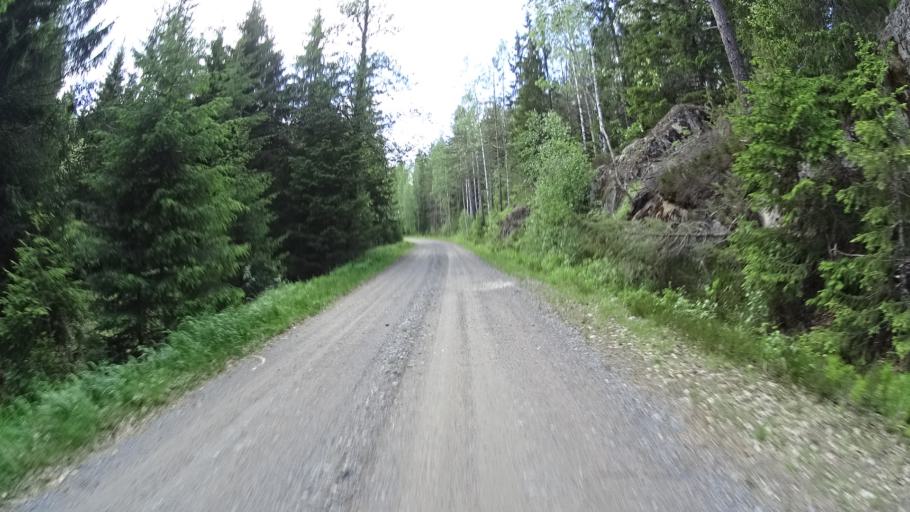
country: FI
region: Varsinais-Suomi
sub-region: Salo
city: Kisko
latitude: 60.1793
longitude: 23.5156
